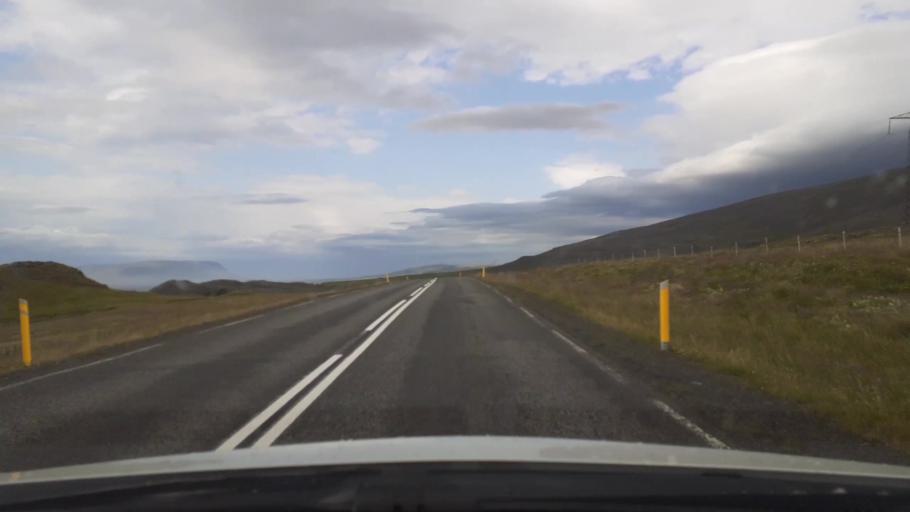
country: IS
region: Capital Region
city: Mosfellsbaer
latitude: 64.3993
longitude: -21.4858
